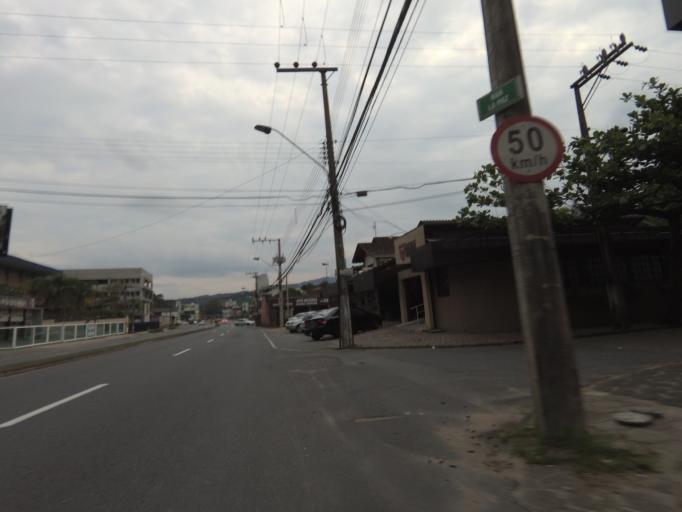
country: BR
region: Santa Catarina
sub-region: Blumenau
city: Blumenau
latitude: -26.9056
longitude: -49.0658
